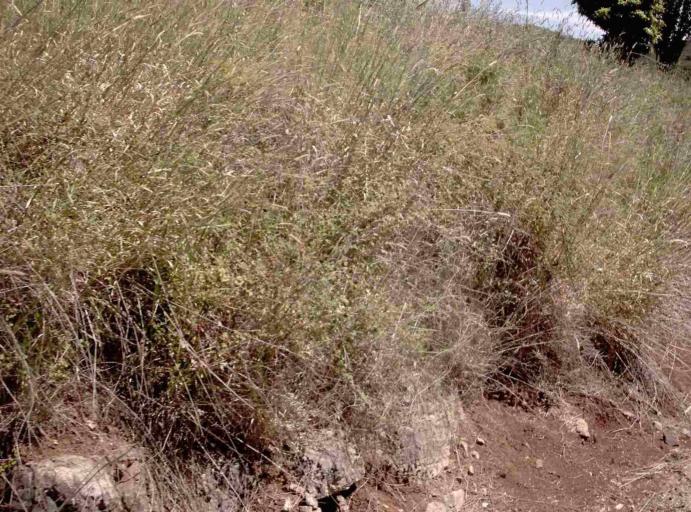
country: AU
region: Victoria
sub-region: East Gippsland
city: Lakes Entrance
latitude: -37.3941
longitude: 148.2173
